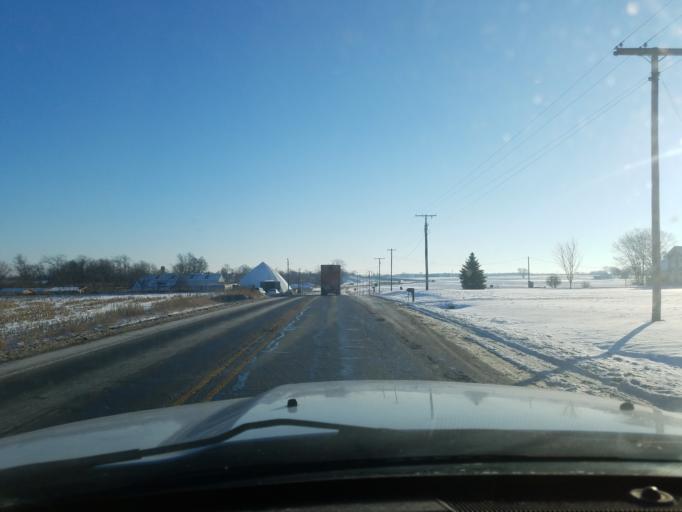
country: US
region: Indiana
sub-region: Noble County
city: Rome City
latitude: 41.4532
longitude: -85.4151
